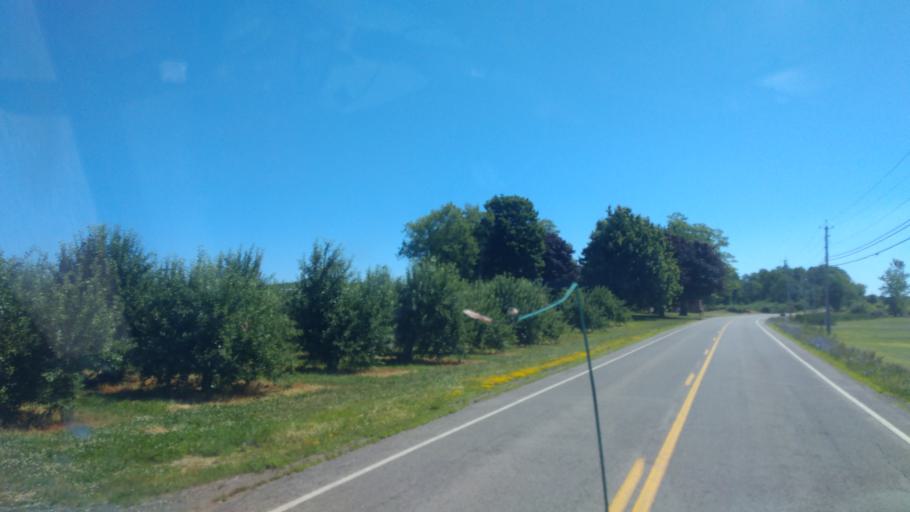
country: US
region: New York
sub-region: Wayne County
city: Williamson
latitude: 43.2830
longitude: -77.1531
